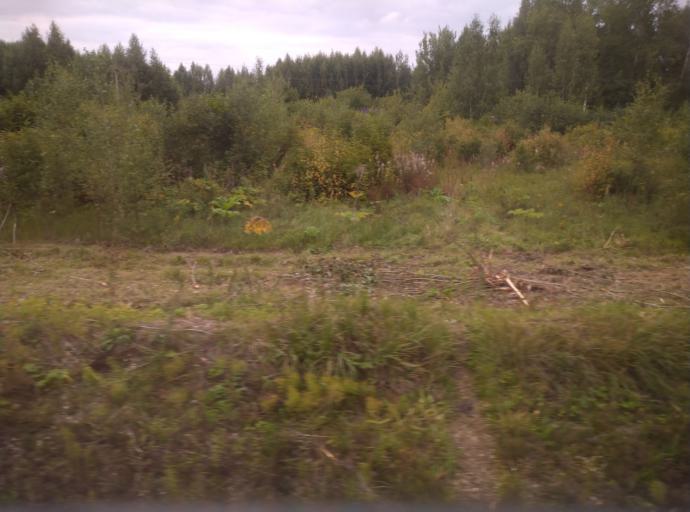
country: RU
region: Jaroslavl
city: Burmakino
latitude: 57.4379
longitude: 40.3836
